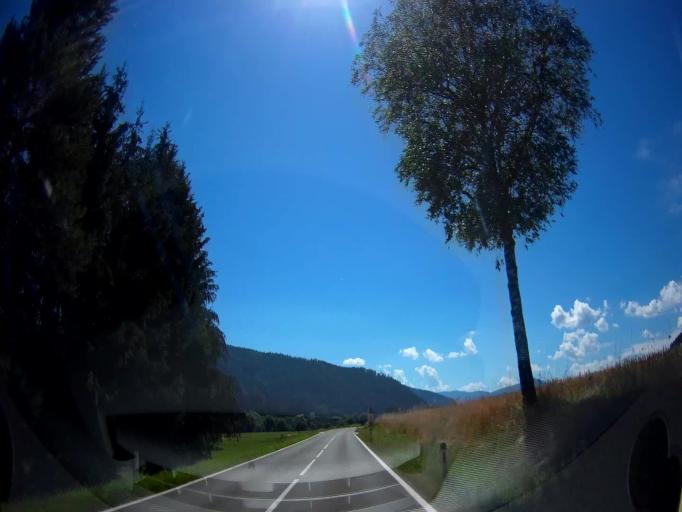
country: AT
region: Carinthia
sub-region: Politischer Bezirk Sankt Veit an der Glan
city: Glodnitz
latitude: 46.8521
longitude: 14.1805
